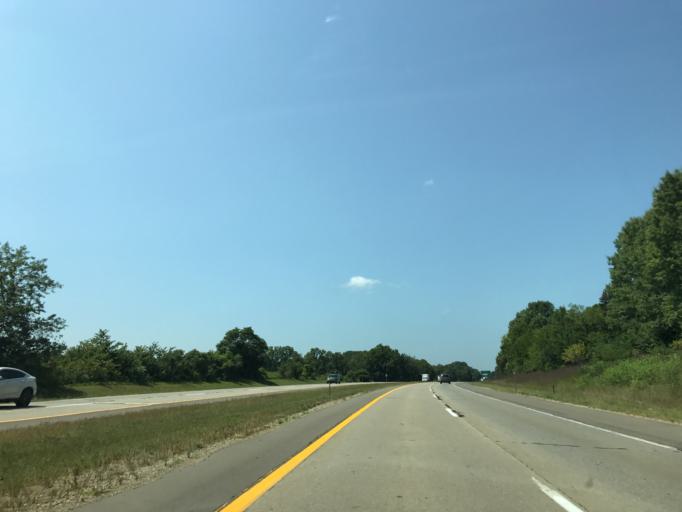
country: US
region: Michigan
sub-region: Berrien County
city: Niles
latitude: 41.8016
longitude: -86.2796
